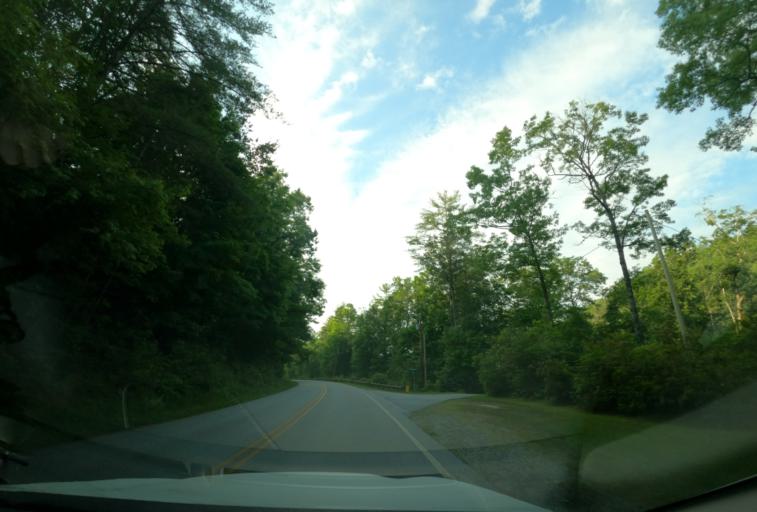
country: US
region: North Carolina
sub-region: Transylvania County
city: Brevard
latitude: 35.2220
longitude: -82.8602
